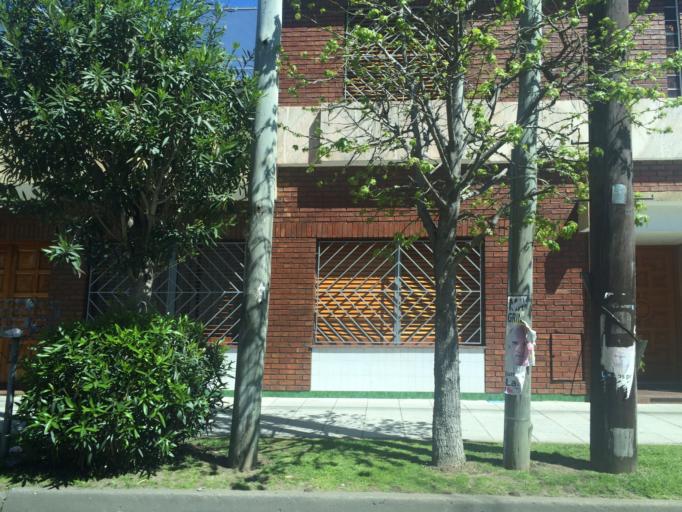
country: AR
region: Buenos Aires
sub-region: Partido de Lanus
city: Lanus
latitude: -34.7142
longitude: -58.3975
